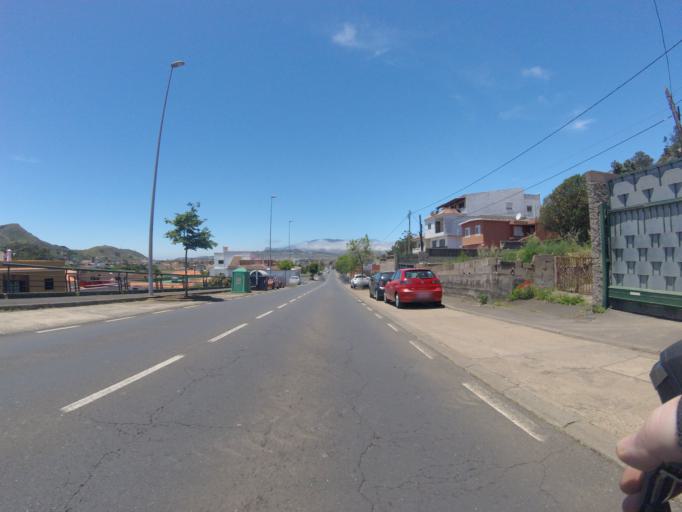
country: ES
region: Canary Islands
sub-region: Provincia de Santa Cruz de Tenerife
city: Tegueste
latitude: 28.5105
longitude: -16.3076
